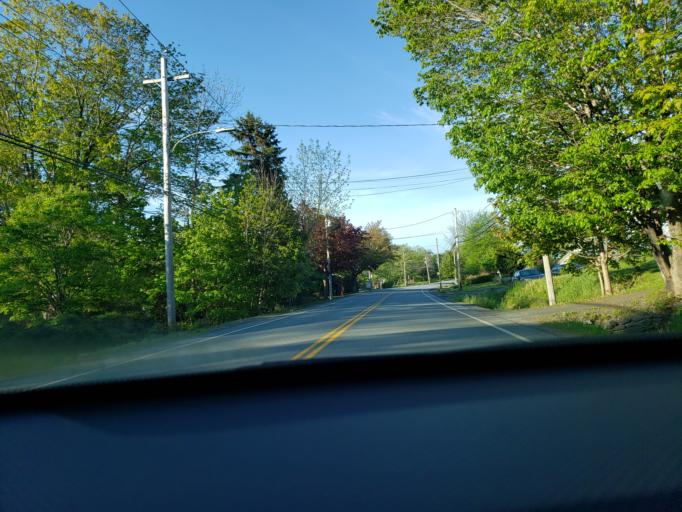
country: CA
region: Nova Scotia
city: Cole Harbour
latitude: 44.7374
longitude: -63.3879
